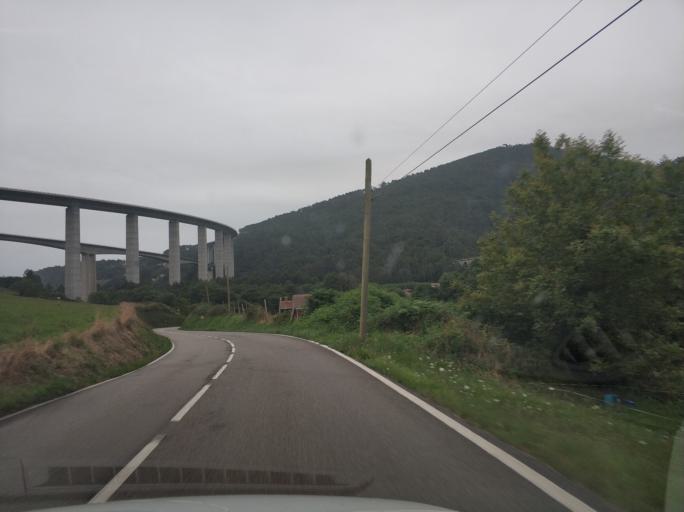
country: ES
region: Asturias
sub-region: Province of Asturias
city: Cudillero
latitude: 43.5527
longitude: -6.1990
